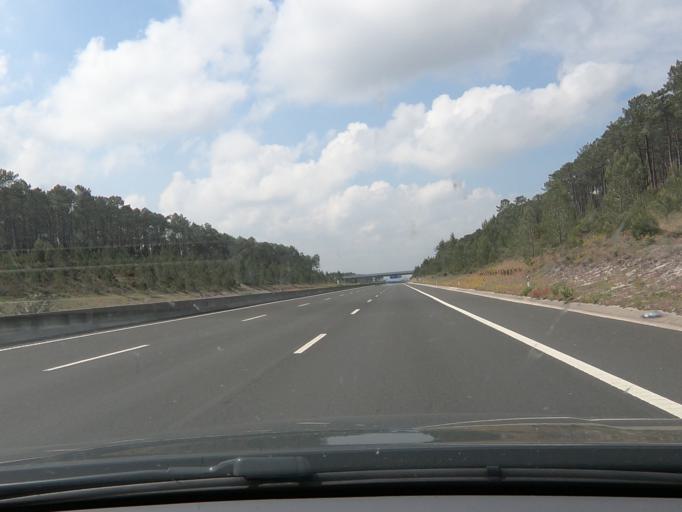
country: PT
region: Leiria
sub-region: Alcobaca
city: Pataias
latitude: 39.6474
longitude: -8.9652
